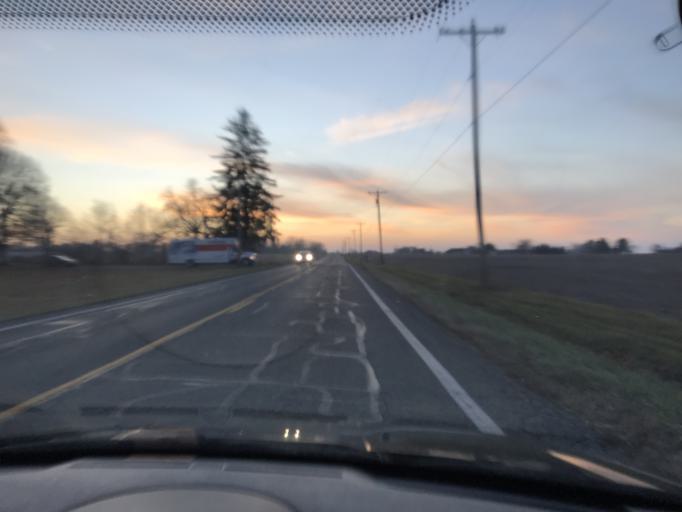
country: US
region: Ohio
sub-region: Champaign County
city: Urbana
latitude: 40.1081
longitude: -83.7055
